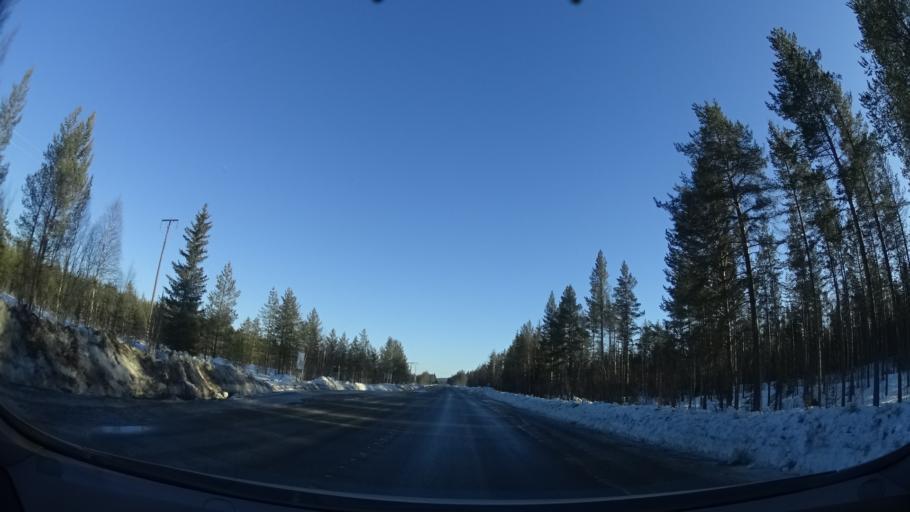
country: SE
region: Vaesterbotten
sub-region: Skelleftea Kommun
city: Langsele
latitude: 65.0524
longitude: 20.0597
